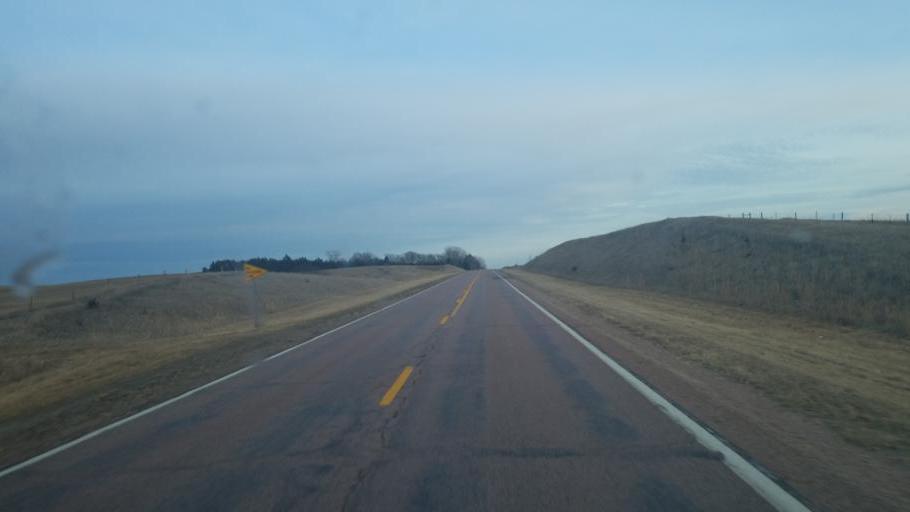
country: US
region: Nebraska
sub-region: Knox County
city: Bloomfield
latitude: 42.7279
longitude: -97.6892
